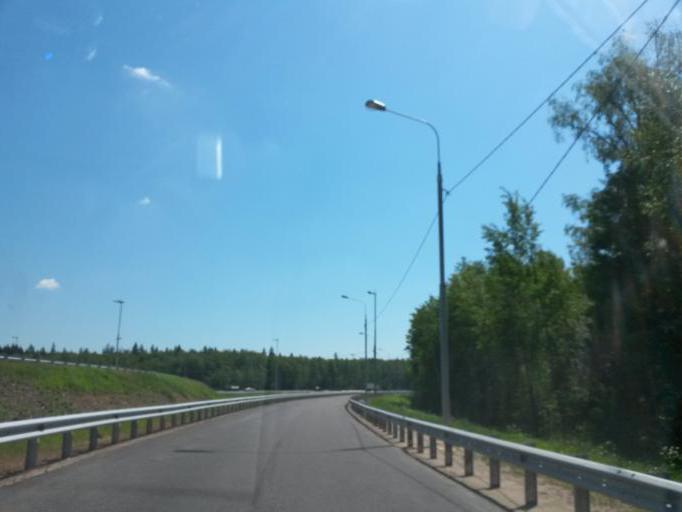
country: RU
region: Moskovskaya
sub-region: Chekhovskiy Rayon
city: Chekhov
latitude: 55.1858
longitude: 37.5317
